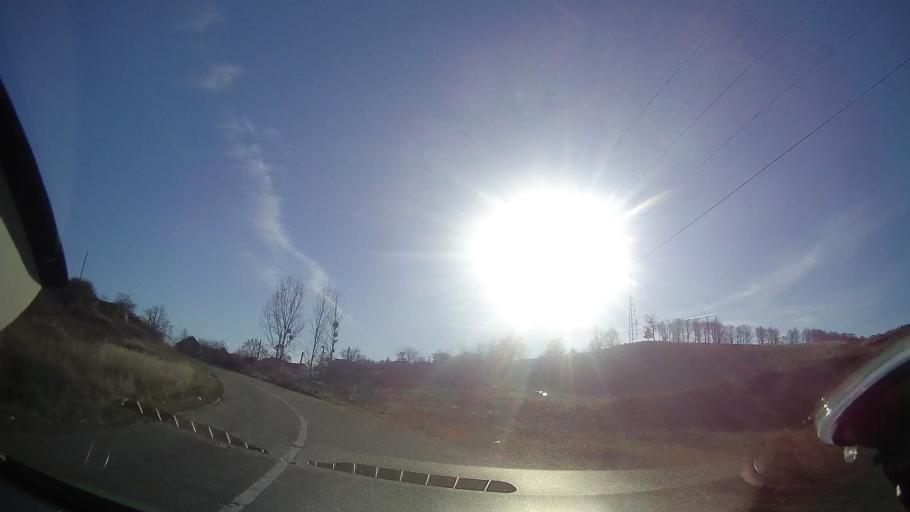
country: RO
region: Bihor
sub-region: Comuna Vadu Crisului
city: Vadu Crisului
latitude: 46.9772
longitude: 22.5341
